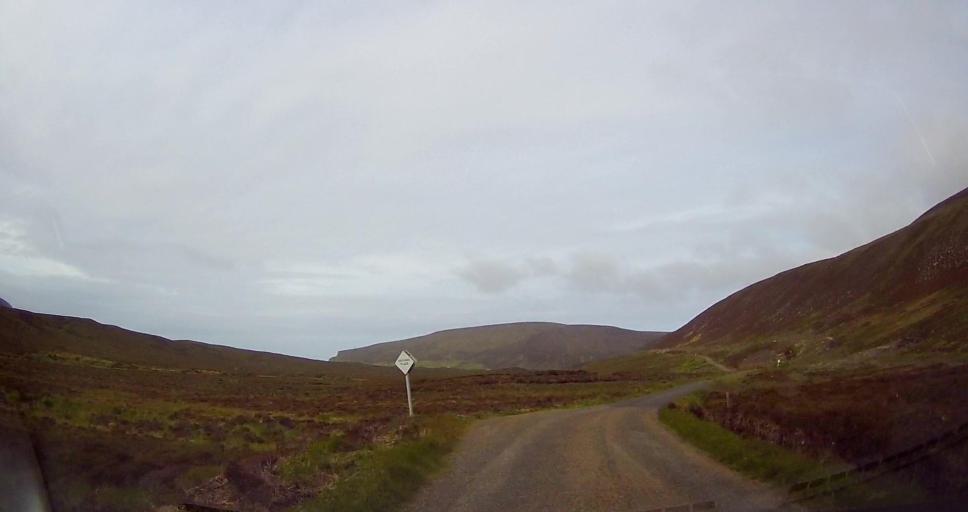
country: GB
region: Scotland
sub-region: Orkney Islands
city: Stromness
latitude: 58.8815
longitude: -3.3481
